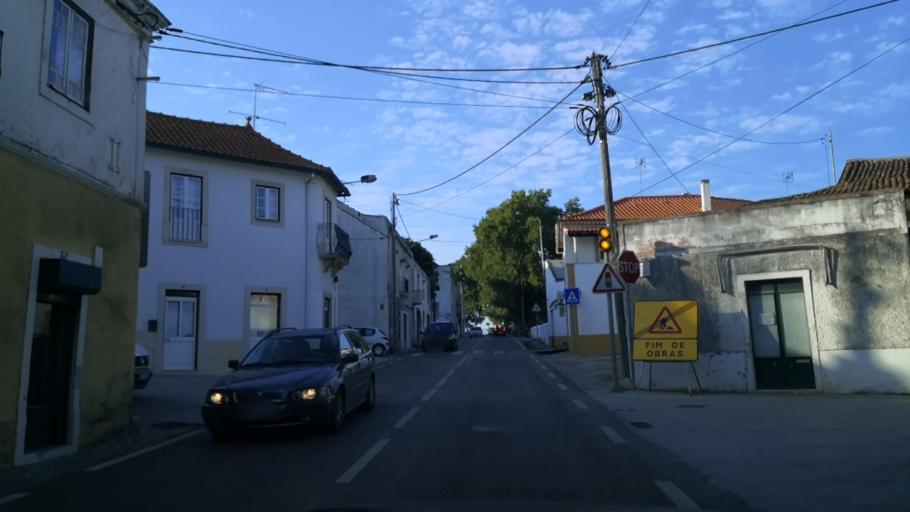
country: PT
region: Santarem
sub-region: Alcanena
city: Alcanena
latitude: 39.3859
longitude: -8.6597
